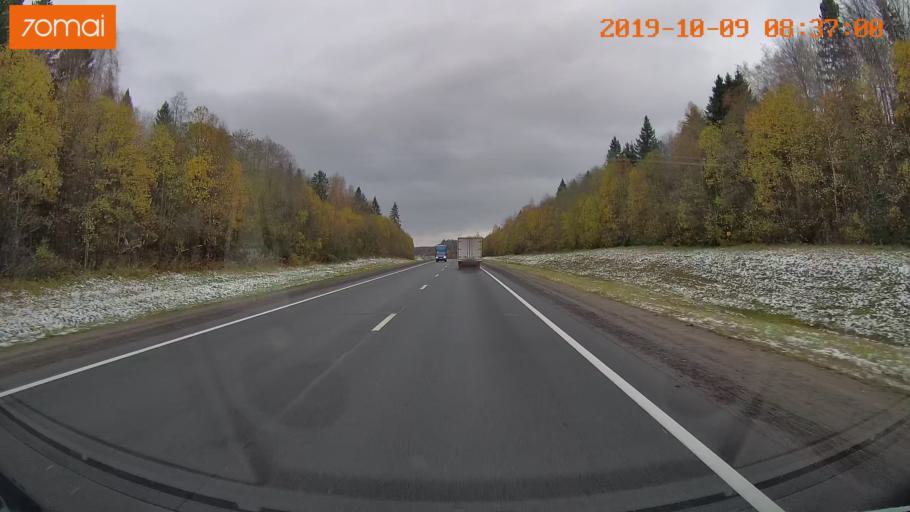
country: RU
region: Vologda
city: Gryazovets
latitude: 58.9348
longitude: 40.1756
